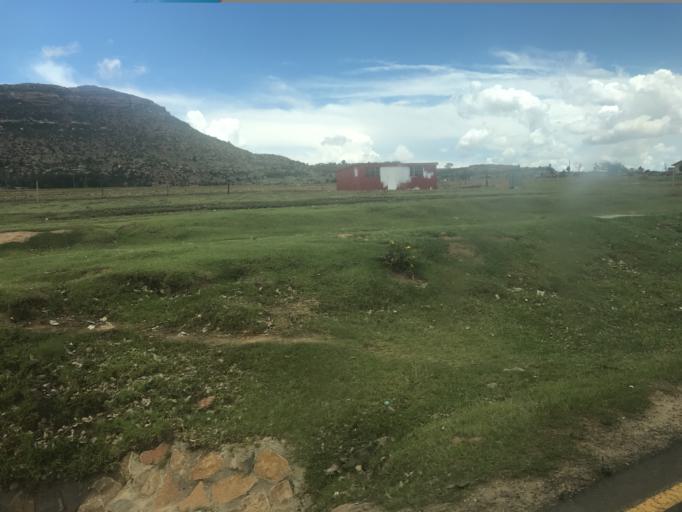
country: LS
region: Maseru
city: Nako
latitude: -29.6235
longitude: 27.4986
